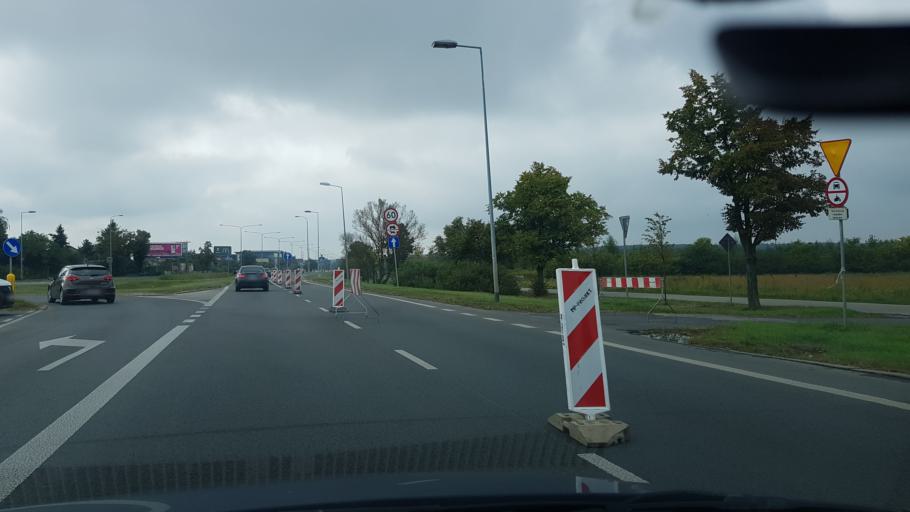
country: PL
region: Masovian Voivodeship
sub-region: Warszawa
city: Kabaty
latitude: 52.1346
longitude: 21.0998
